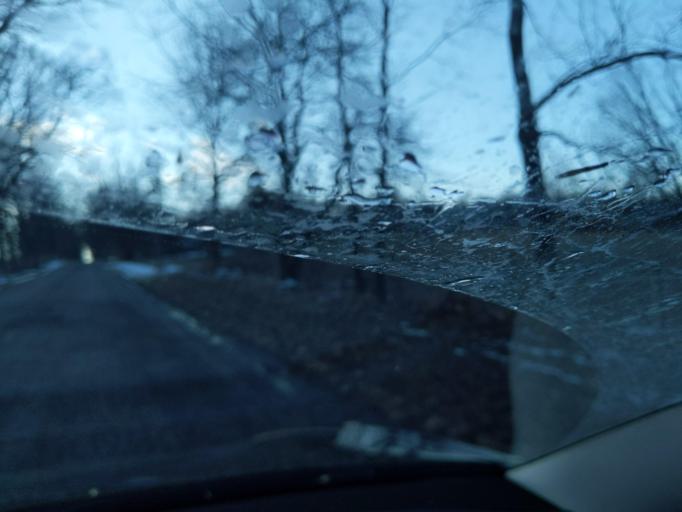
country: US
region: Michigan
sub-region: Ingham County
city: Stockbridge
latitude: 42.5179
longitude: -84.1677
